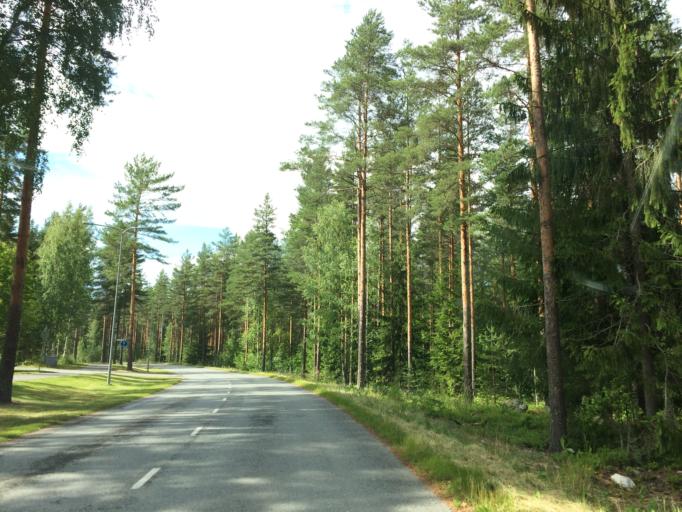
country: FI
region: Haeme
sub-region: Haemeenlinna
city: Turenki
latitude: 60.9386
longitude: 24.6478
